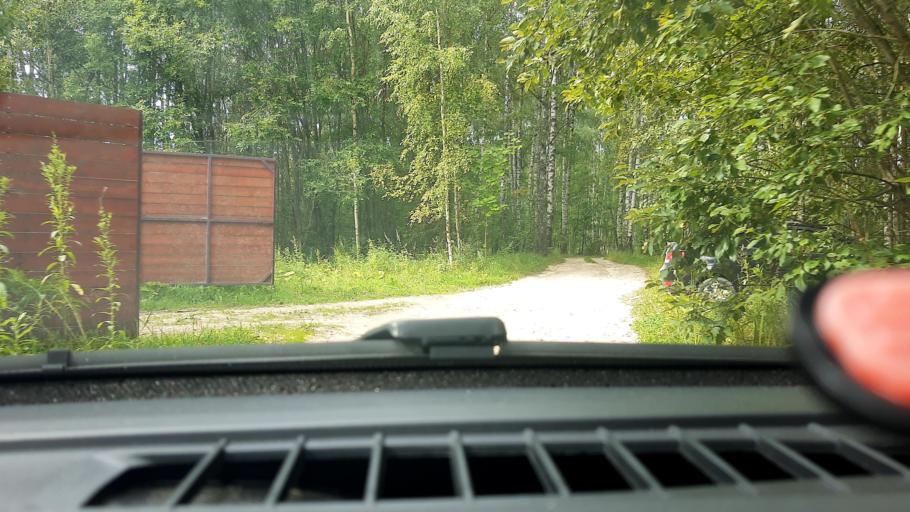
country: RU
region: Nizjnij Novgorod
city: Burevestnik
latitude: 56.0178
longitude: 43.7213
